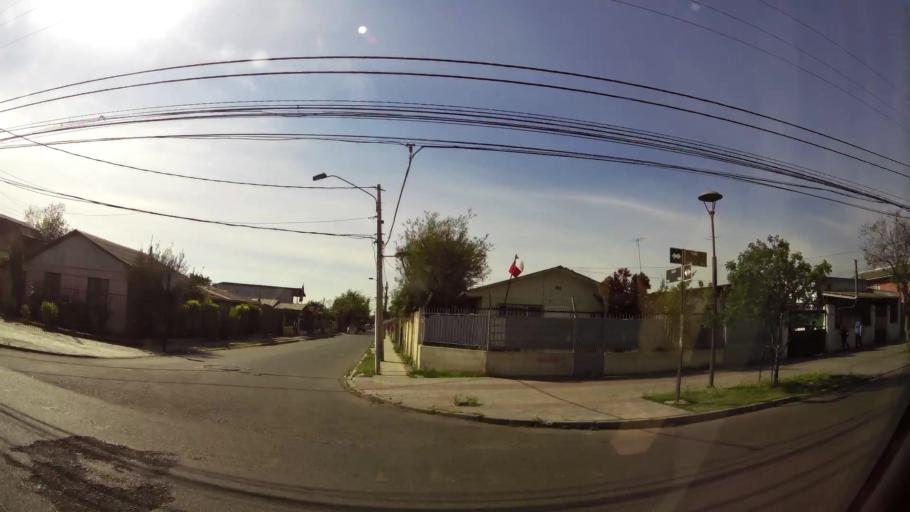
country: CL
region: Santiago Metropolitan
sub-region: Provincia de Santiago
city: La Pintana
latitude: -33.5328
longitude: -70.6321
